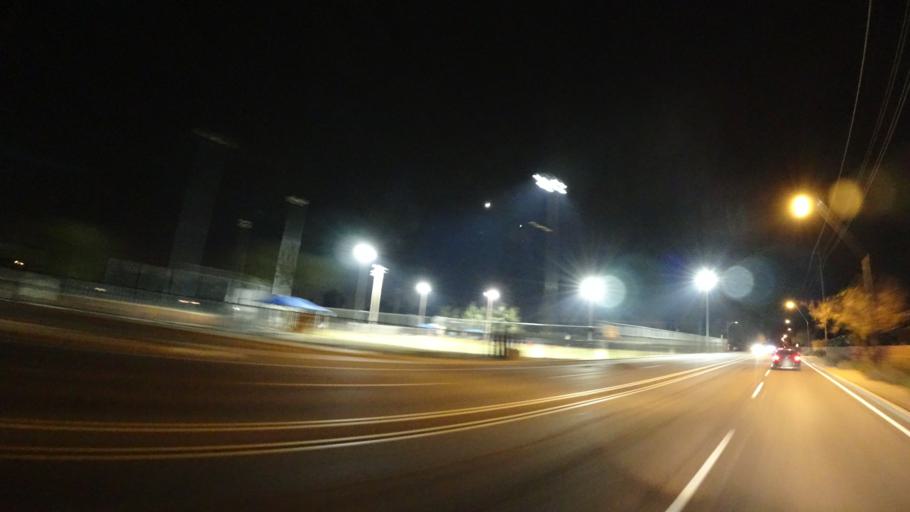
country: US
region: Arizona
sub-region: Maricopa County
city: Paradise Valley
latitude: 33.4899
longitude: -111.9648
